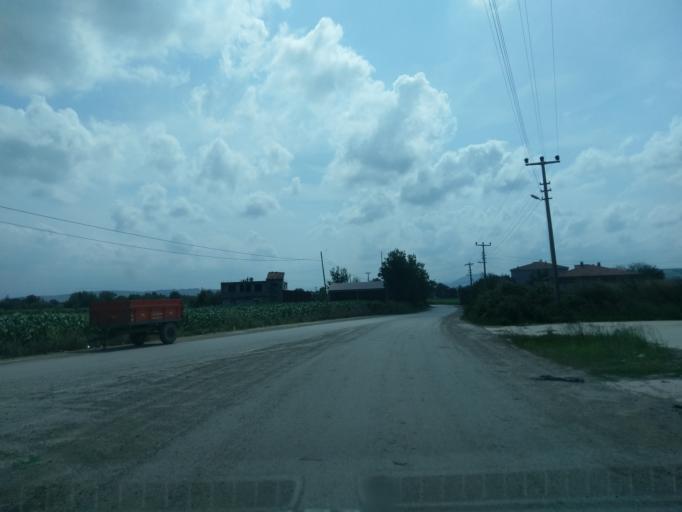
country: TR
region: Samsun
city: Bafra
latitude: 41.5776
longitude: 35.8517
